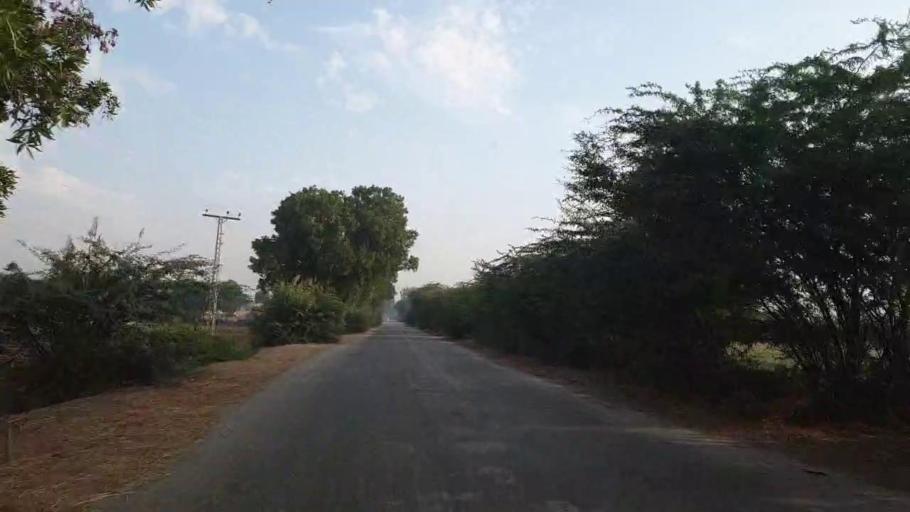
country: PK
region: Sindh
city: Tando Bago
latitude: 24.7555
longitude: 68.9518
